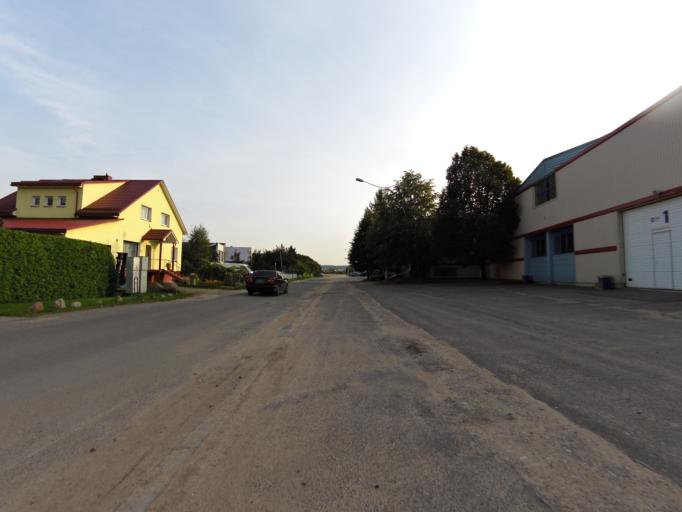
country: LT
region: Vilnius County
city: Vilkpede
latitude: 54.6798
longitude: 25.2270
